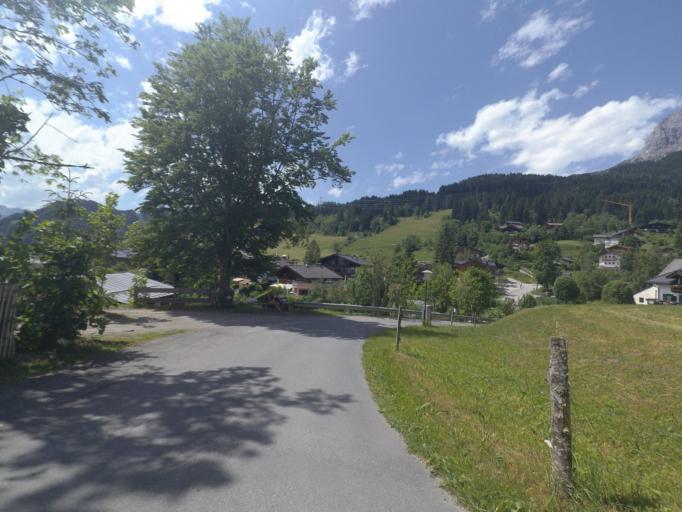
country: AT
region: Salzburg
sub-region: Politischer Bezirk Zell am See
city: Dienten am Hochkonig
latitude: 47.4110
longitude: 12.9797
